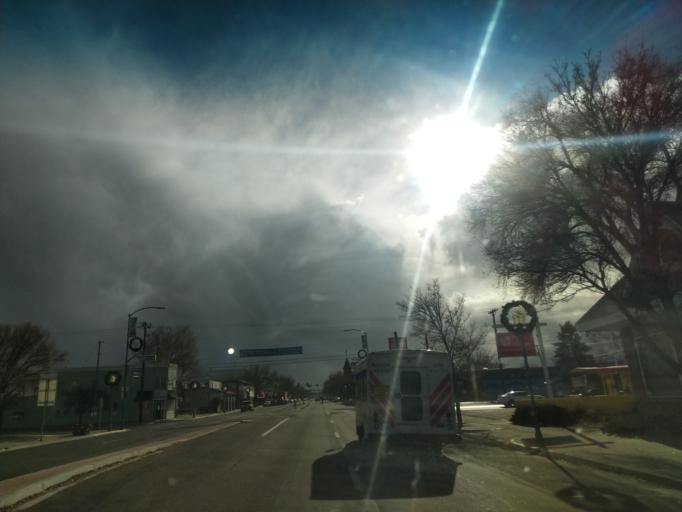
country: US
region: Colorado
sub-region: Delta County
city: Delta
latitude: 38.7449
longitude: -108.0709
